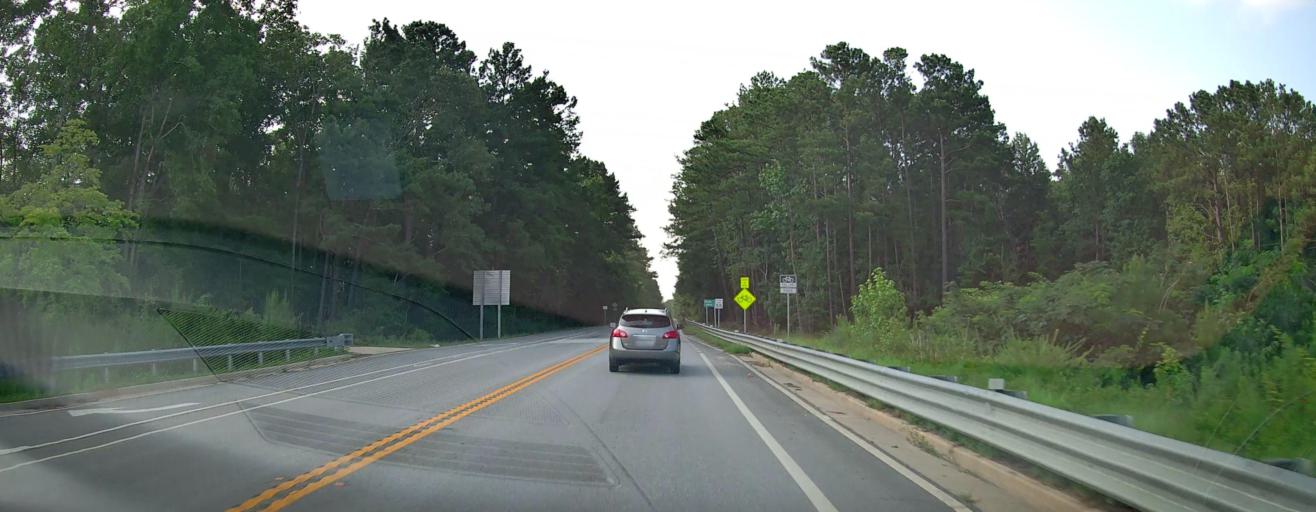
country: US
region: Georgia
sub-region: Monroe County
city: Forsyth
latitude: 33.0252
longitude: -83.7453
